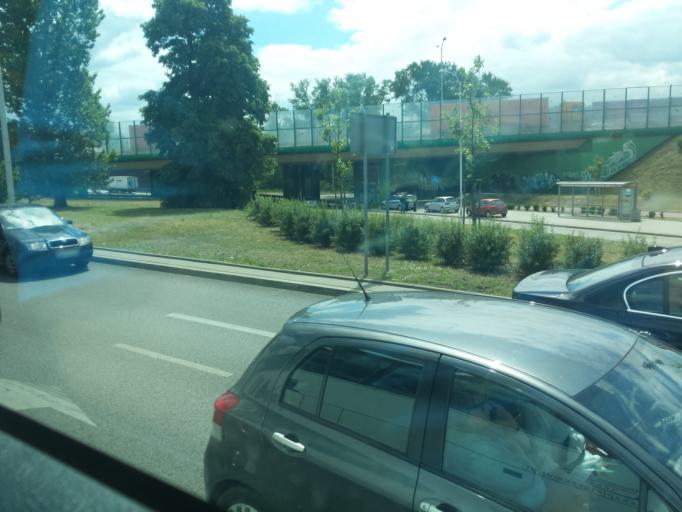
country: PL
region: Masovian Voivodeship
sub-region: Warszawa
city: Rembertow
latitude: 52.2334
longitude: 21.1289
